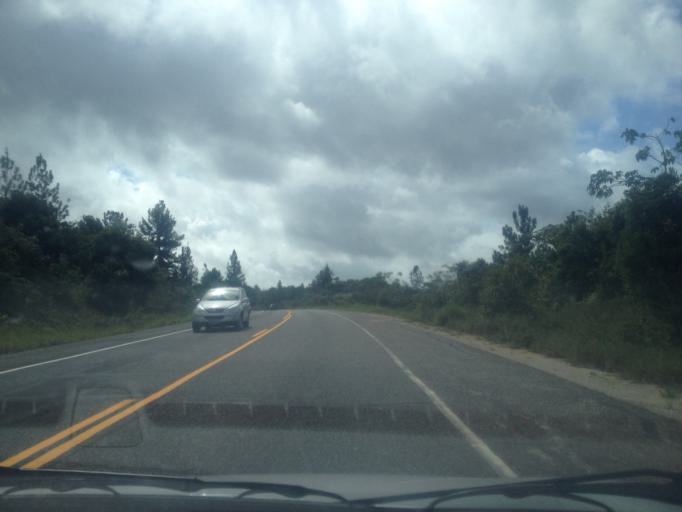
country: BR
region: Bahia
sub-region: Entre Rios
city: Entre Rios
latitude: -12.1430
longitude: -37.7927
